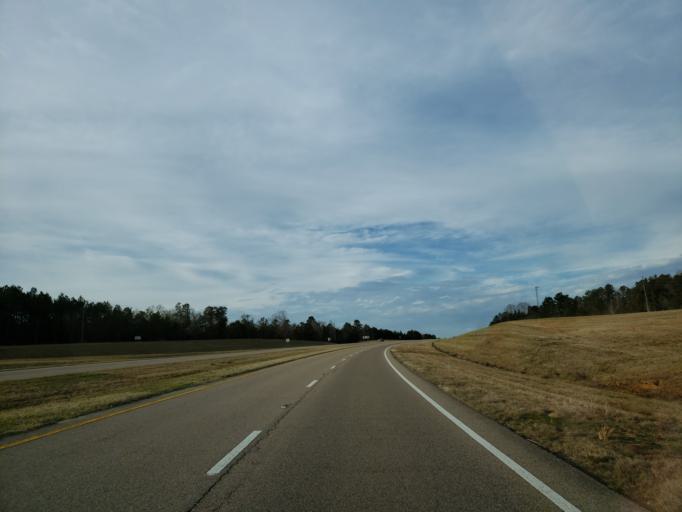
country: US
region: Mississippi
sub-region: Wayne County
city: Waynesboro
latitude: 31.6830
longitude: -88.6161
